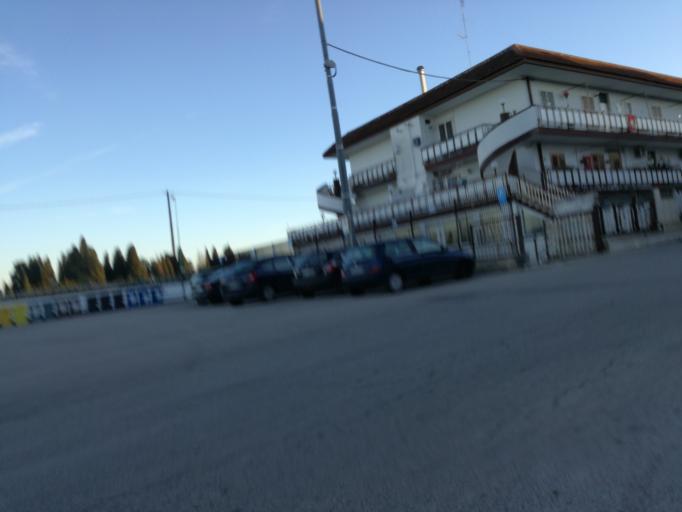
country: IT
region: Apulia
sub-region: Provincia di Bari
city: Adelfia
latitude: 41.0024
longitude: 16.8810
